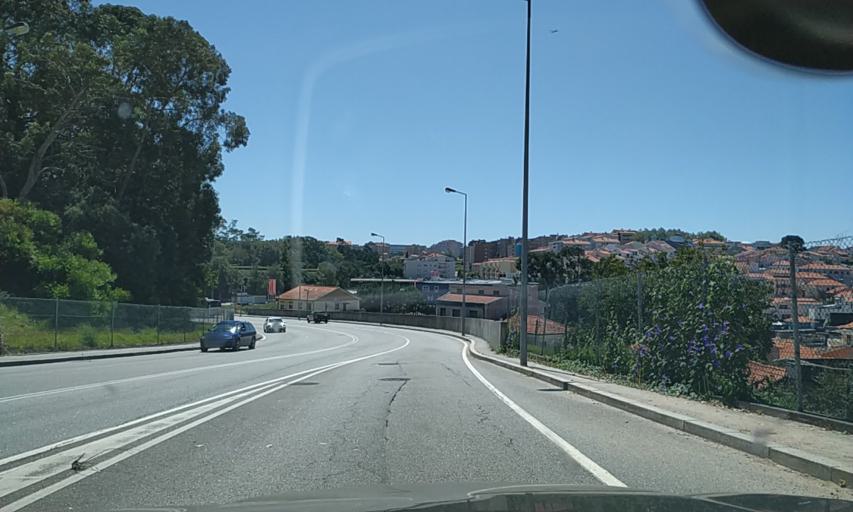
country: PT
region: Porto
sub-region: Vila Nova de Gaia
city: Canidelo
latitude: 41.1411
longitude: -8.6421
